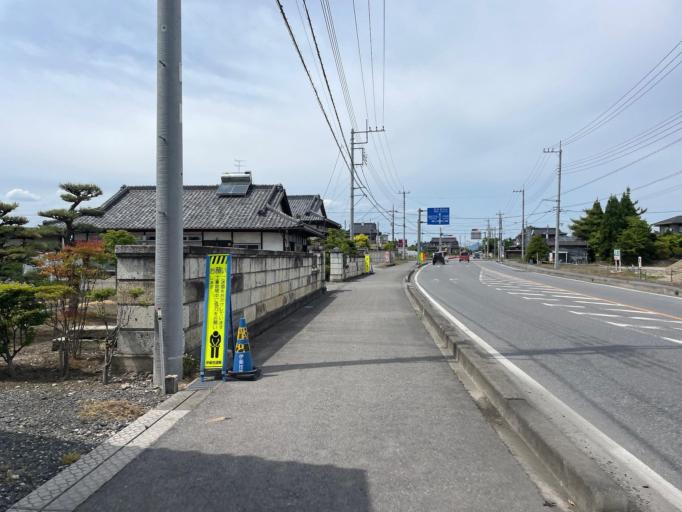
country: JP
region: Tochigi
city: Mibu
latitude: 36.4721
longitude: 139.7646
